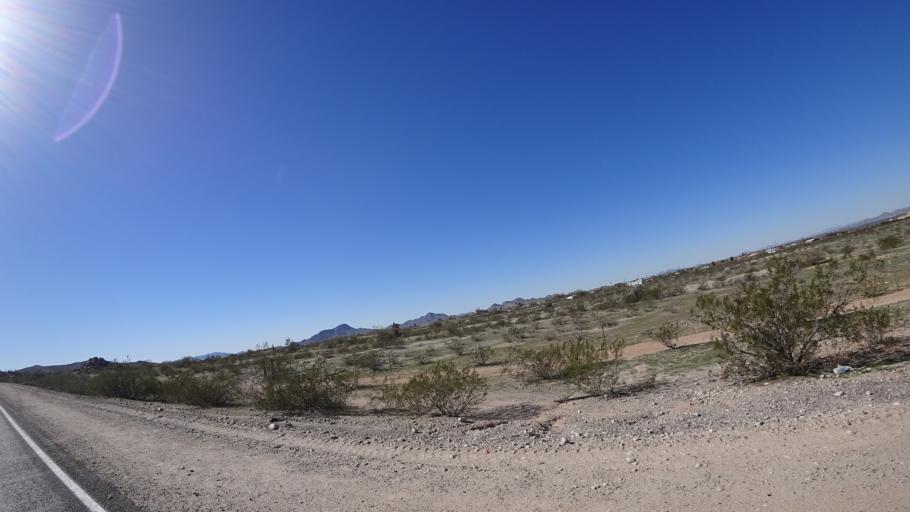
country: US
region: Arizona
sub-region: Maricopa County
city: Buckeye
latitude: 33.3309
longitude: -112.4700
